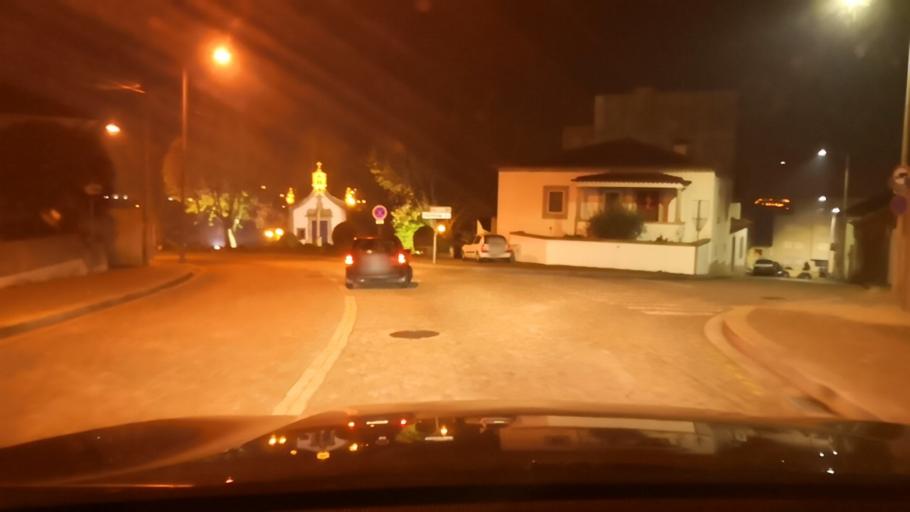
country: PT
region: Porto
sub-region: Maia
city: Maia
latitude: 41.2331
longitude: -8.6295
